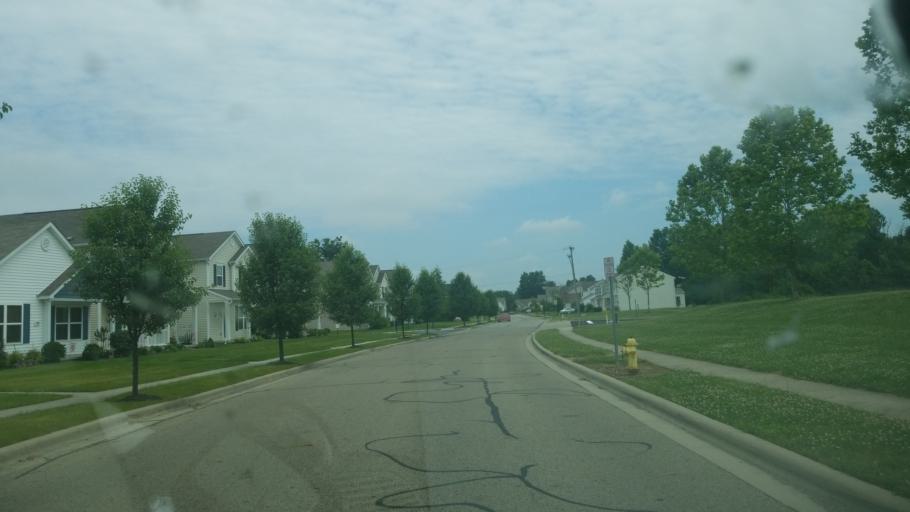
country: US
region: Ohio
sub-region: Franklin County
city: Reynoldsburg
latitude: 40.0130
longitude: -82.7829
